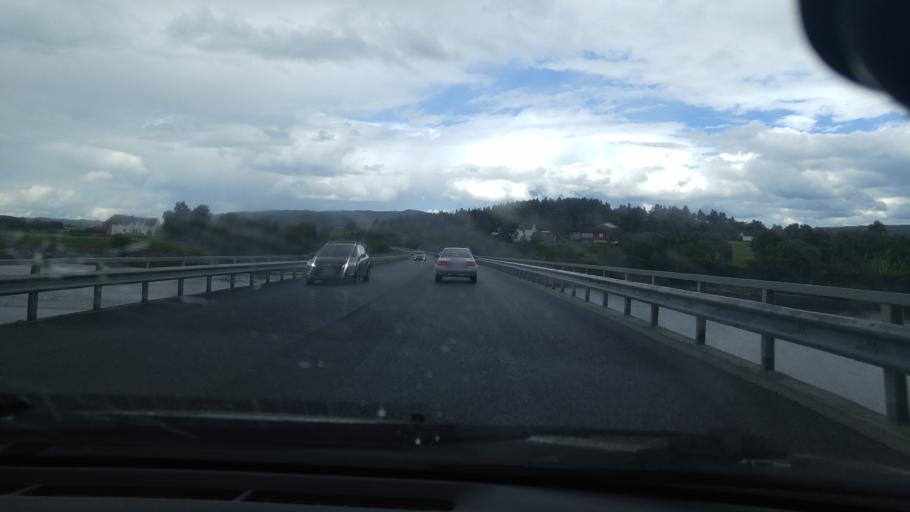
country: NO
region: Nord-Trondelag
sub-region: Verdal
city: Verdal
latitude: 63.8029
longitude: 11.4593
